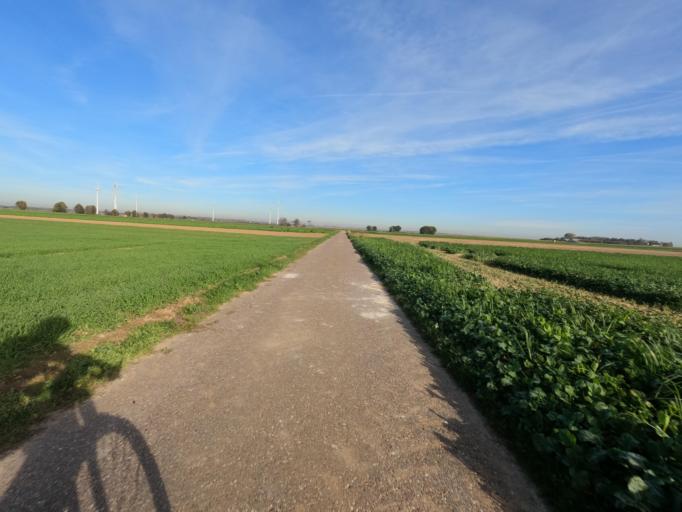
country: DE
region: North Rhine-Westphalia
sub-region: Regierungsbezirk Koln
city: Titz
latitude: 51.0537
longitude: 6.4089
